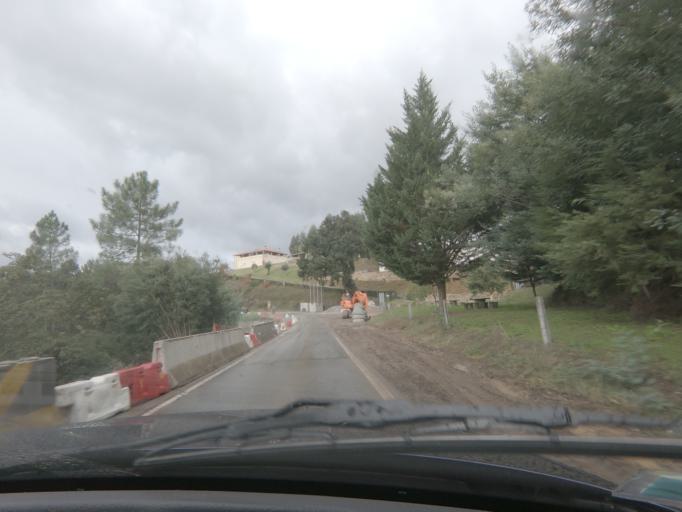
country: PT
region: Vila Real
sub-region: Mondim de Basto
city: Mondim de Basto
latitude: 41.4095
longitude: -7.9700
